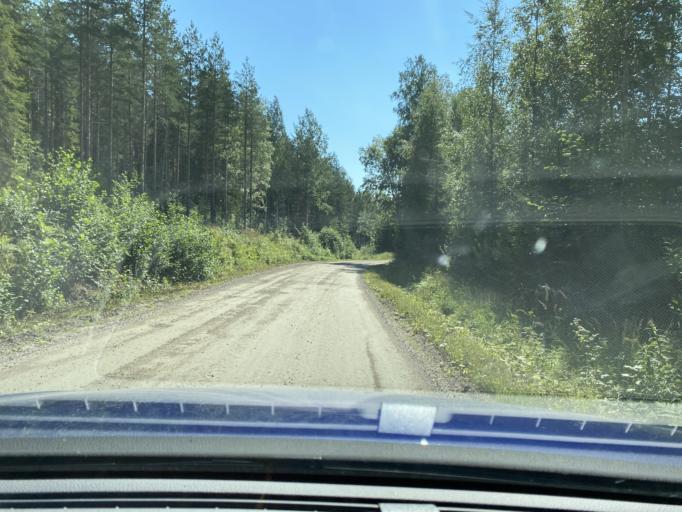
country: FI
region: Central Finland
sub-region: Jyvaeskylae
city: Korpilahti
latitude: 61.8709
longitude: 25.4193
